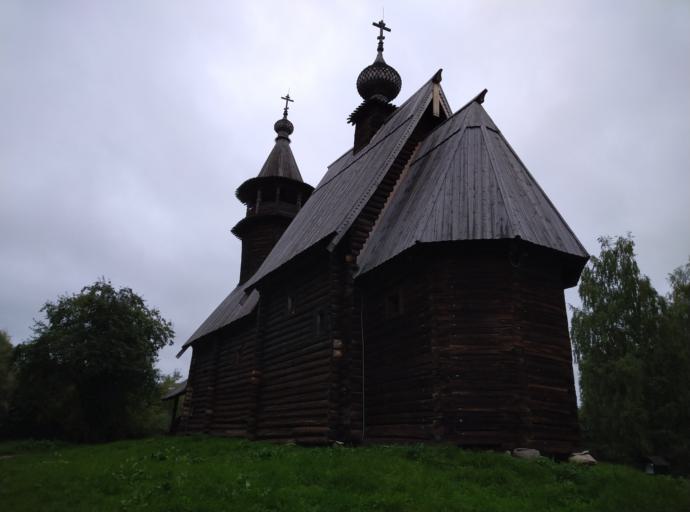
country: RU
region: Kostroma
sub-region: Kostromskoy Rayon
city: Kostroma
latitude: 57.7746
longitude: 40.8899
